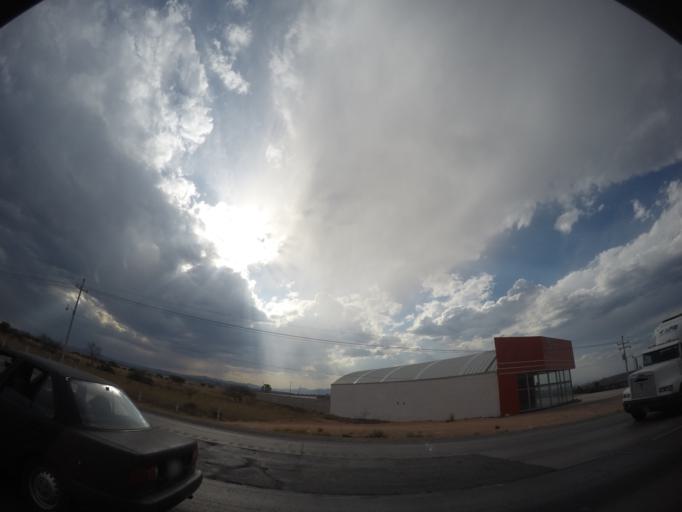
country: MX
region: Mexico
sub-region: Jilotepec
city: La Comunidad
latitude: 20.0619
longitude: -99.5978
